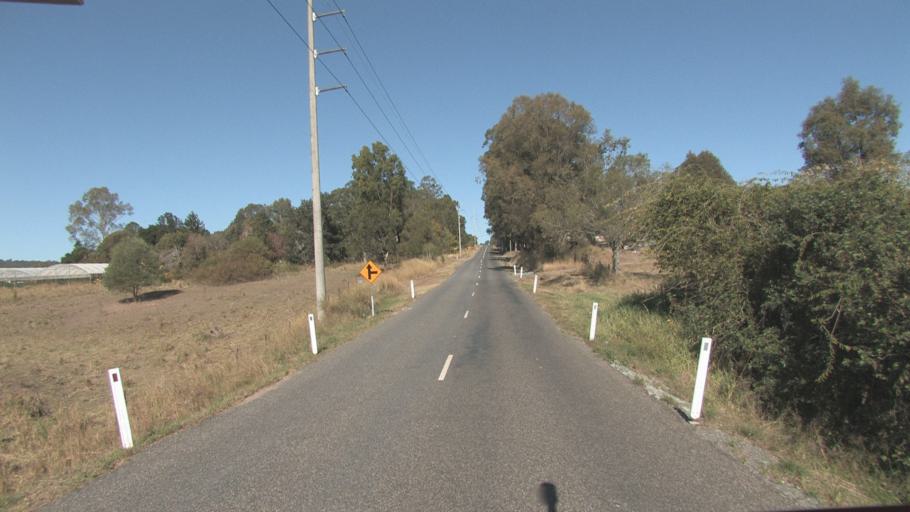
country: AU
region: Queensland
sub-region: Logan
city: Cedar Vale
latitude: -27.8737
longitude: 153.0170
